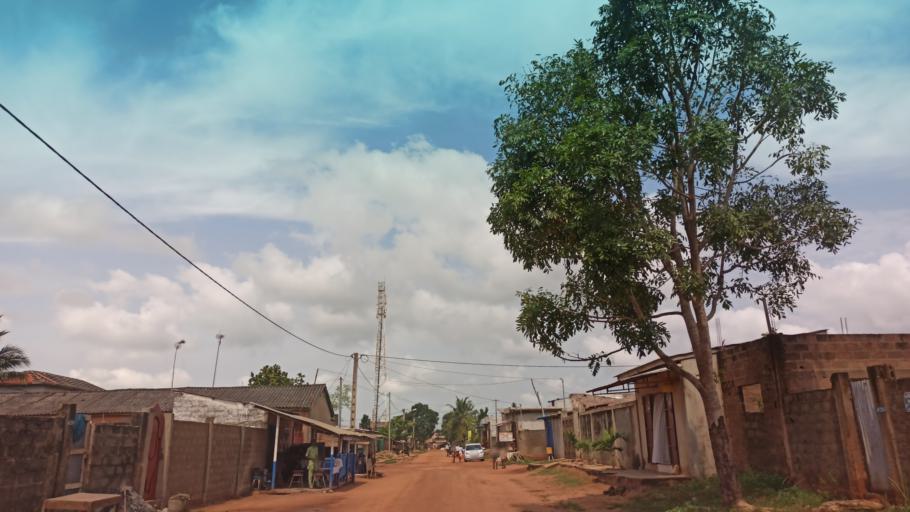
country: BJ
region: Queme
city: Porto-Novo
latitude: 6.4991
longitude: 2.5876
